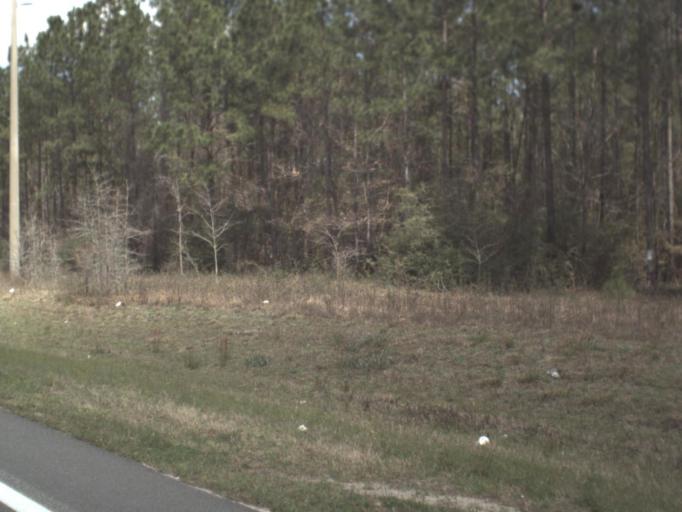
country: US
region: Florida
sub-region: Wakulla County
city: Crawfordville
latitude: 30.2514
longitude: -84.3623
